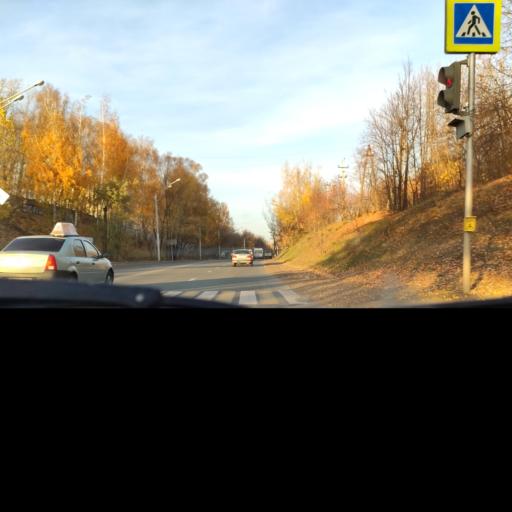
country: RU
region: Bashkortostan
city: Avdon
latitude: 54.6812
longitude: 55.8080
